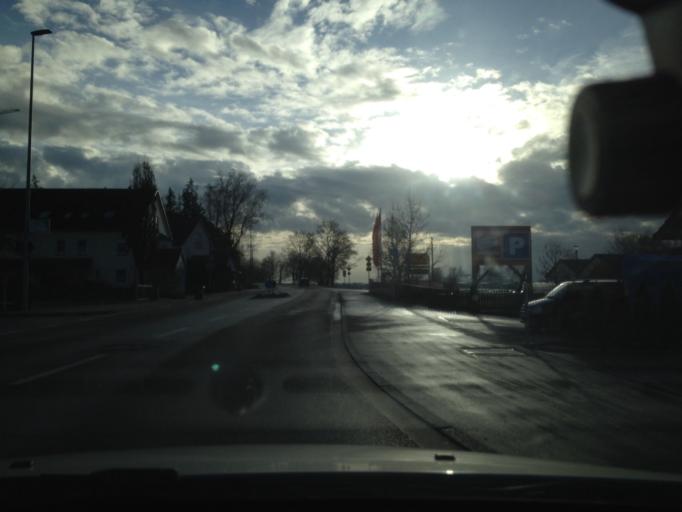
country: DE
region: Bavaria
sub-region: Swabia
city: Grossaitingen
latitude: 48.2216
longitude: 10.7772
